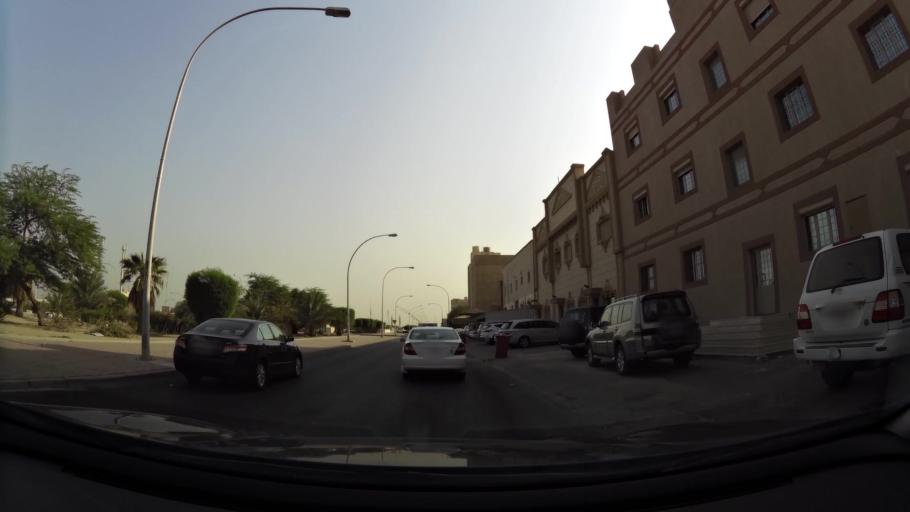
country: KW
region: Al Ahmadi
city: Ar Riqqah
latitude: 29.1172
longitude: 48.1051
